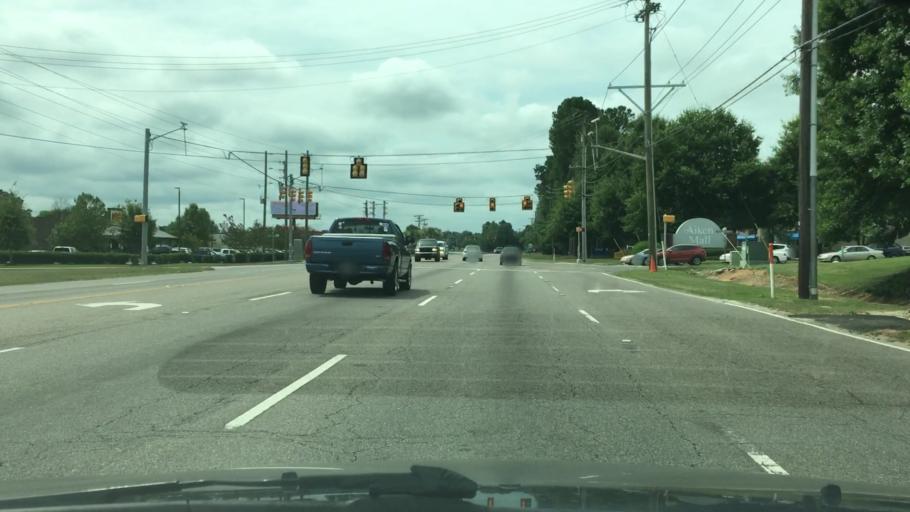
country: US
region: South Carolina
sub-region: Aiken County
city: Aiken
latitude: 33.5118
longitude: -81.7135
